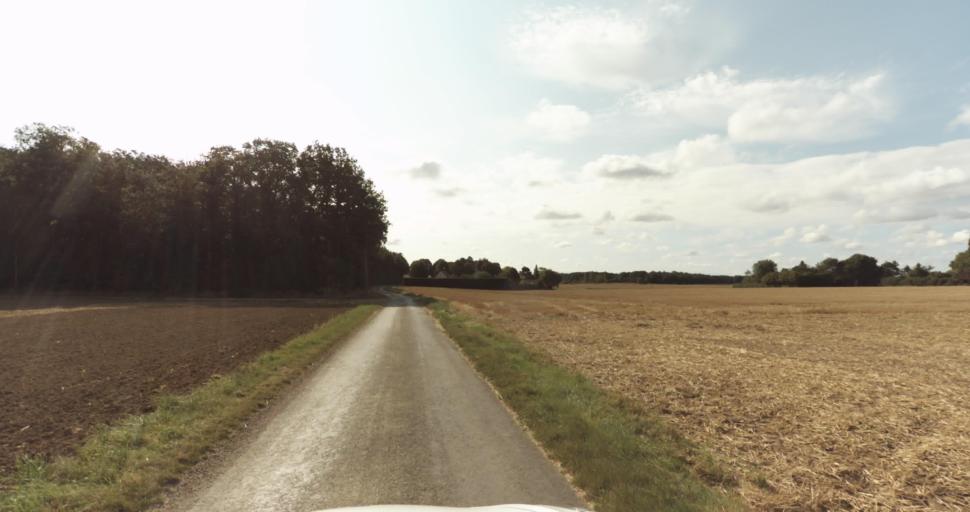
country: FR
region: Haute-Normandie
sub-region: Departement de l'Eure
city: Tillieres-sur-Avre
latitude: 48.7754
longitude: 1.0836
